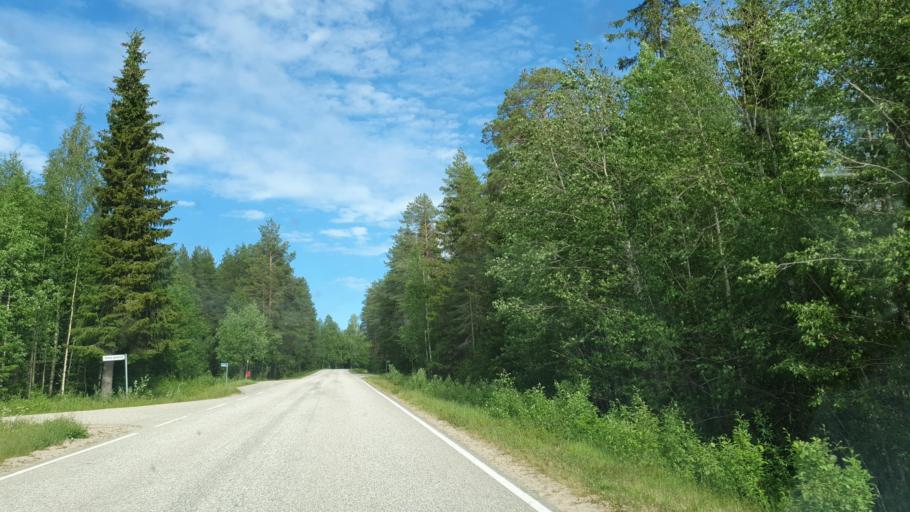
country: FI
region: Kainuu
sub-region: Kehys-Kainuu
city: Suomussalmi
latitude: 64.5730
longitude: 29.0031
